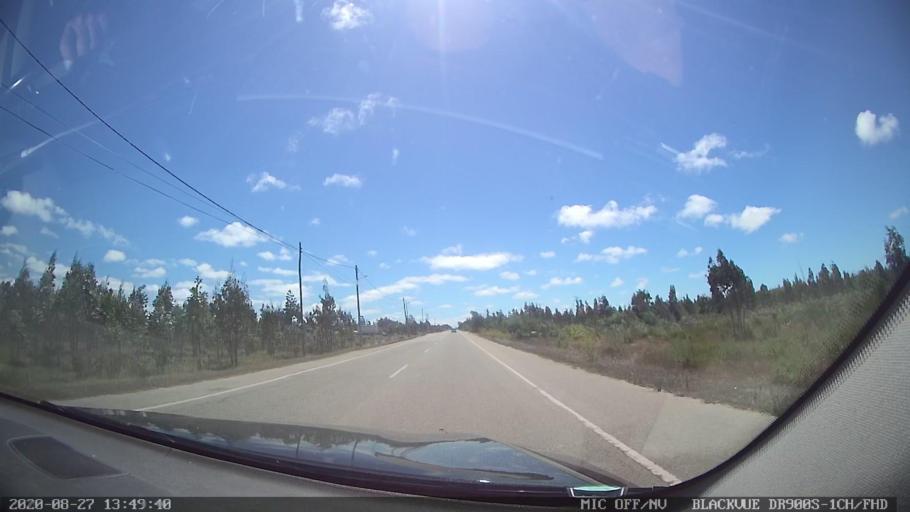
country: PT
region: Coimbra
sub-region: Mira
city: Mira
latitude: 40.3653
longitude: -8.7466
